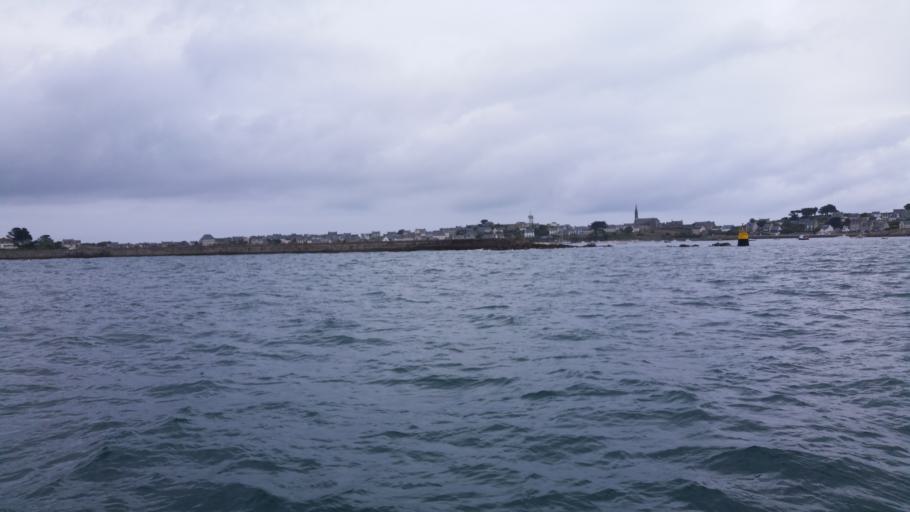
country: FR
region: Brittany
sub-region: Departement du Finistere
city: Roscoff
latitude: 48.7357
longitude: -4.0118
